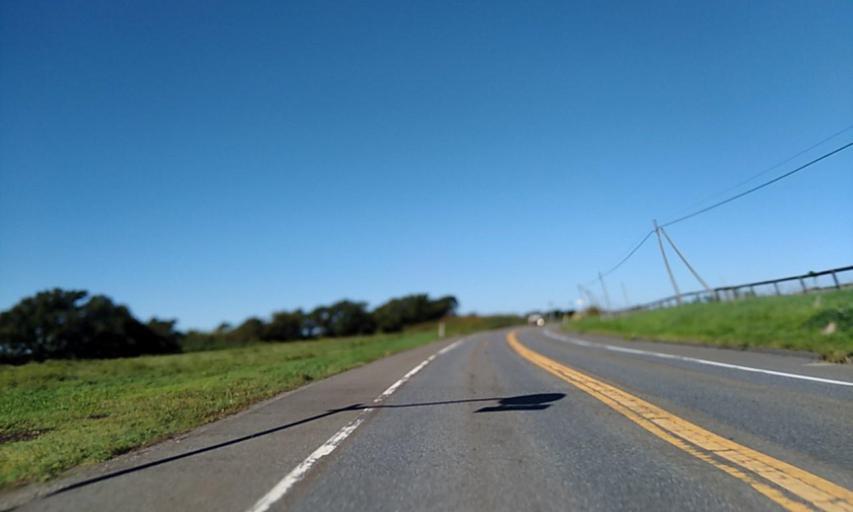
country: JP
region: Hokkaido
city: Shizunai-furukawacho
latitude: 42.4142
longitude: 142.2354
